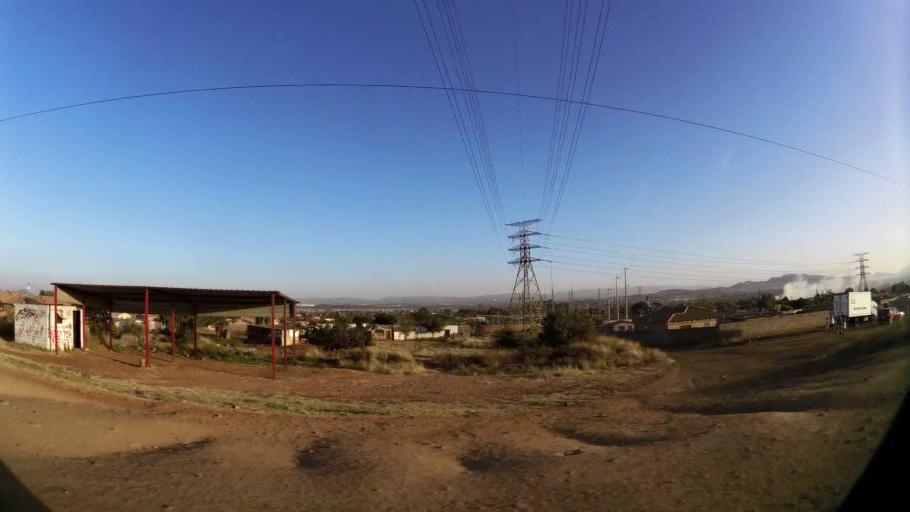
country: ZA
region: Gauteng
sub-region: City of Tshwane Metropolitan Municipality
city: Mabopane
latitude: -25.5762
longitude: 28.0789
